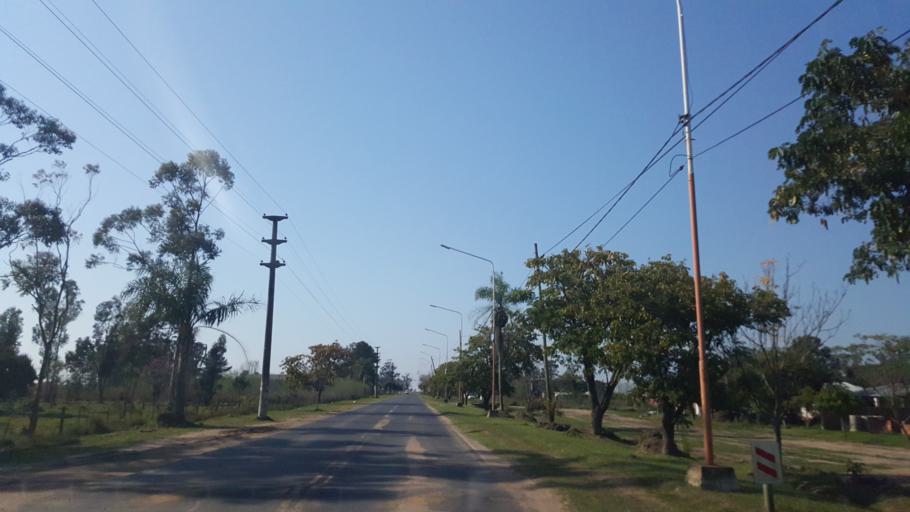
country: AR
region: Corrientes
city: Ituzaingo
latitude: -27.5962
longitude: -56.6776
